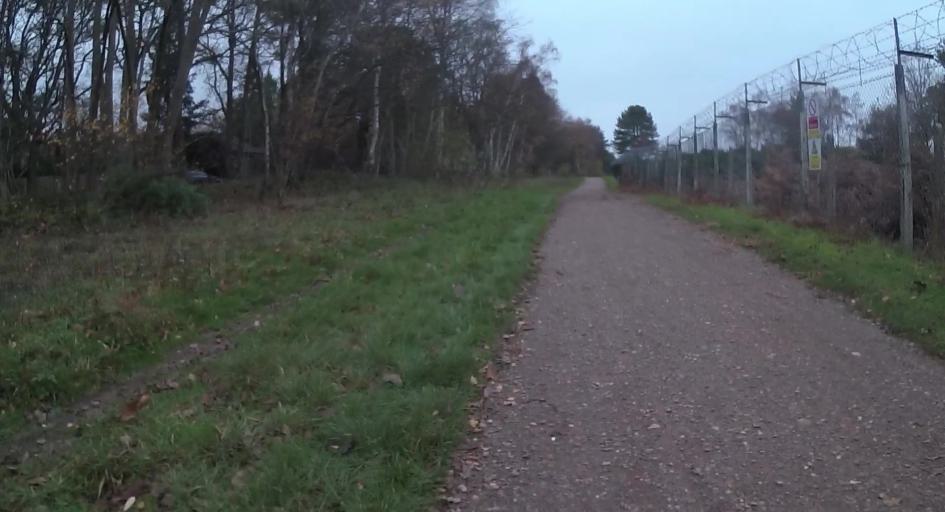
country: GB
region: England
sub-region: Surrey
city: Bagshot
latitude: 51.3325
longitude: -0.6970
